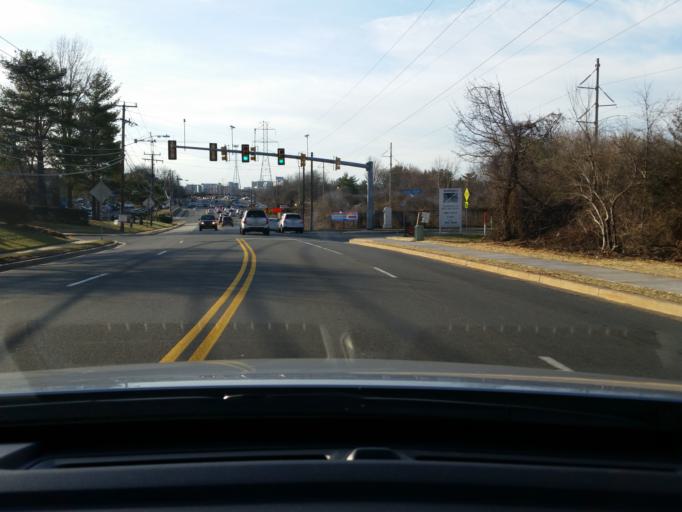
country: US
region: Virginia
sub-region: Fairfax County
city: Reston
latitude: 38.9490
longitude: -77.3321
